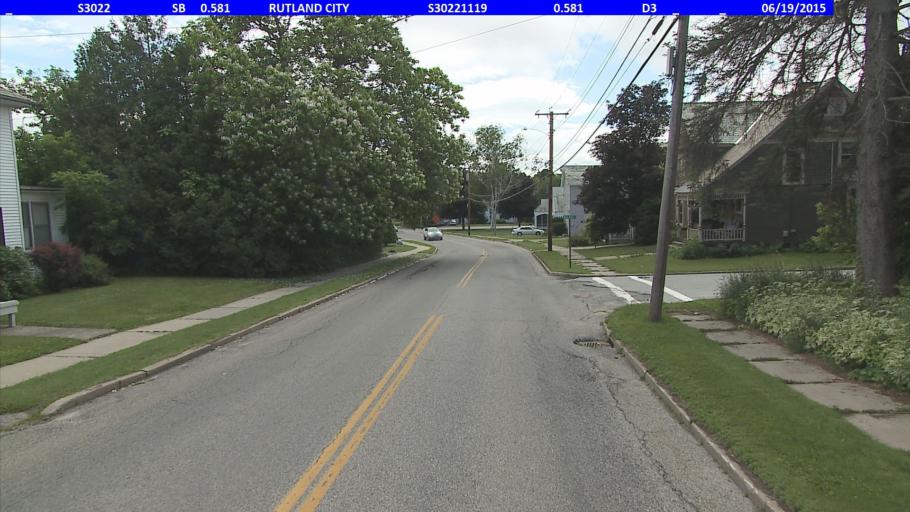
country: US
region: Vermont
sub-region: Rutland County
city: Rutland
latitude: 43.6171
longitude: -72.9844
